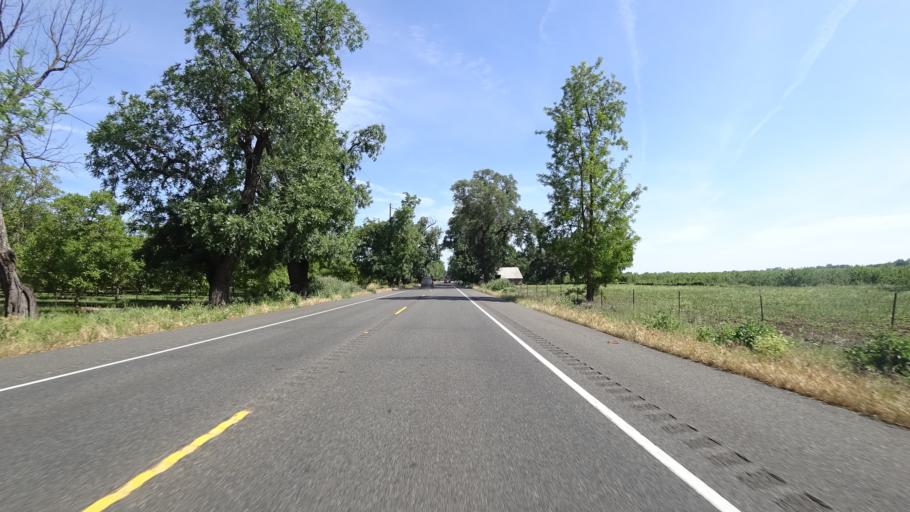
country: US
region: California
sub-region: Tehama County
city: Red Bluff
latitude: 40.1752
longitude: -122.1677
